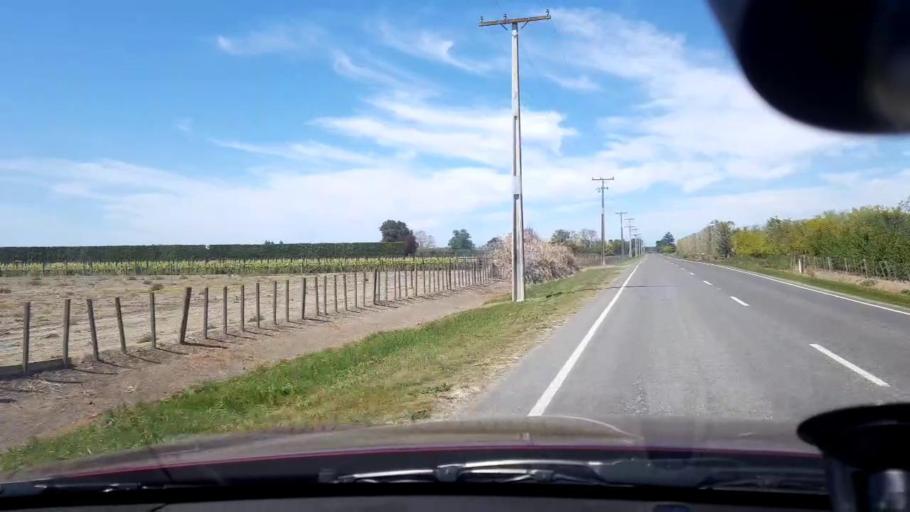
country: NZ
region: Gisborne
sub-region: Gisborne District
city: Gisborne
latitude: -38.6318
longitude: 177.9278
